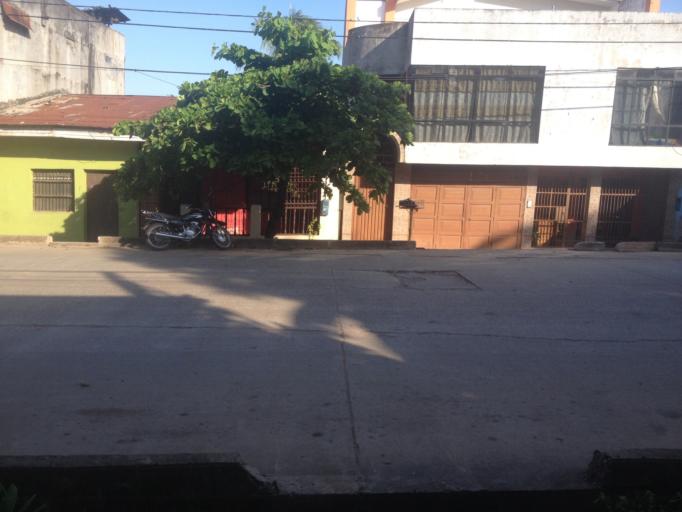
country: PE
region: Ucayali
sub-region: Provincia de Coronel Portillo
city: Pucallpa
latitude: -8.3810
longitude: -74.5274
